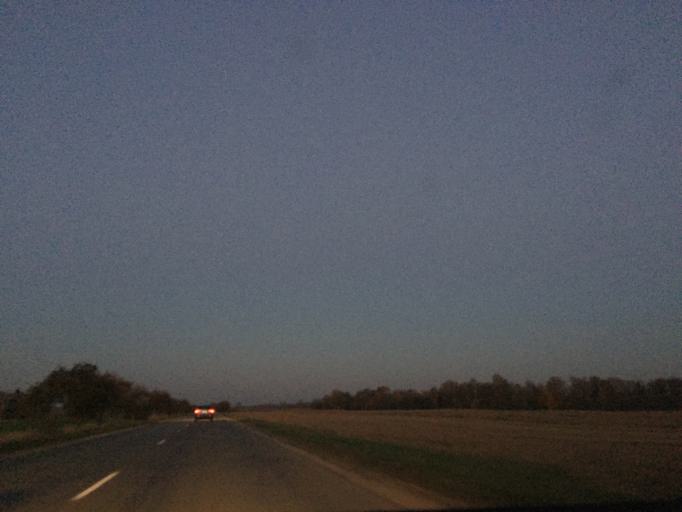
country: LT
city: Zagare
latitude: 56.4884
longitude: 23.2097
